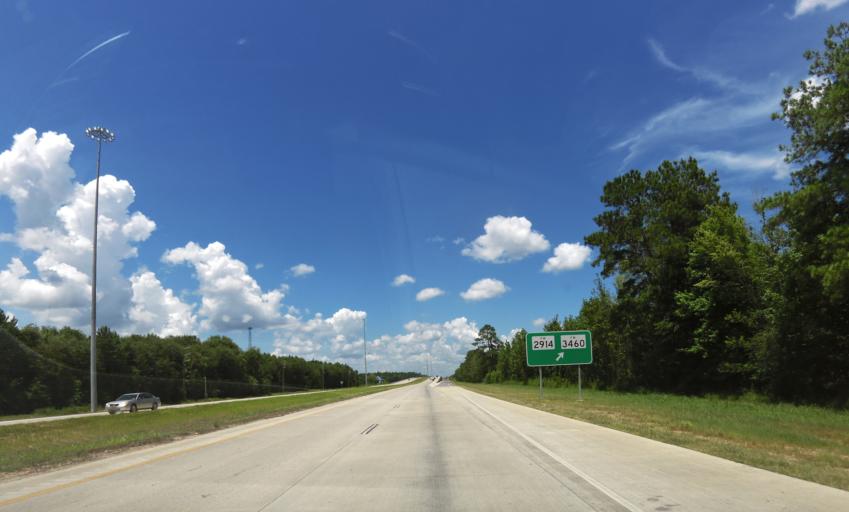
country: US
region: Texas
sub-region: San Jacinto County
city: Shepherd
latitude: 30.4394
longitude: -95.0327
